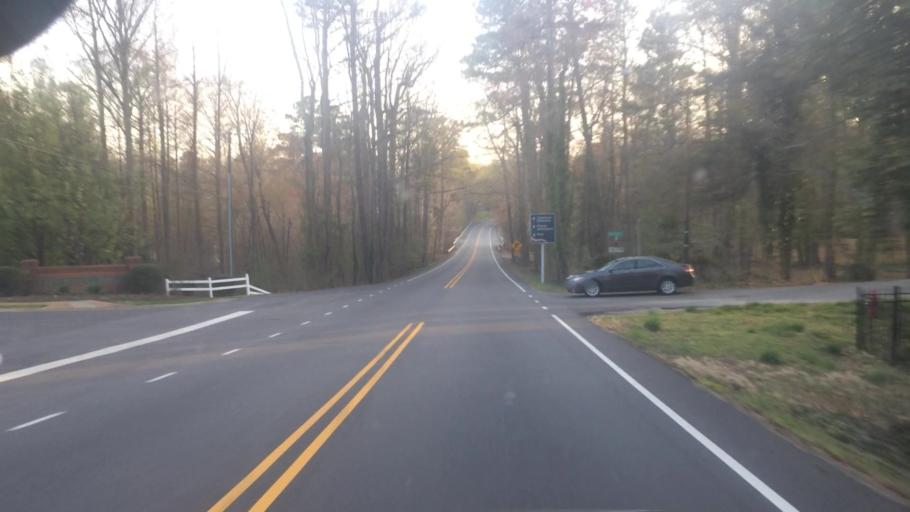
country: US
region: Virginia
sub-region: James City County
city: Williamsburg
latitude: 37.2400
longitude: -76.7454
